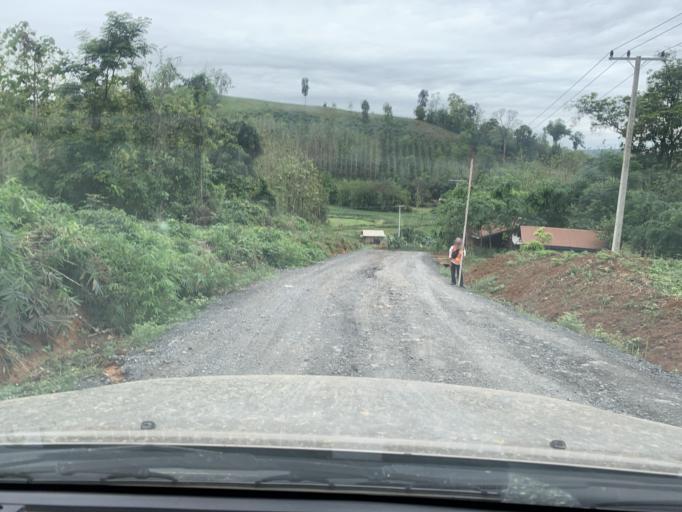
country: TH
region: Nan
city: Mae Charim
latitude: 18.4181
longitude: 101.4649
